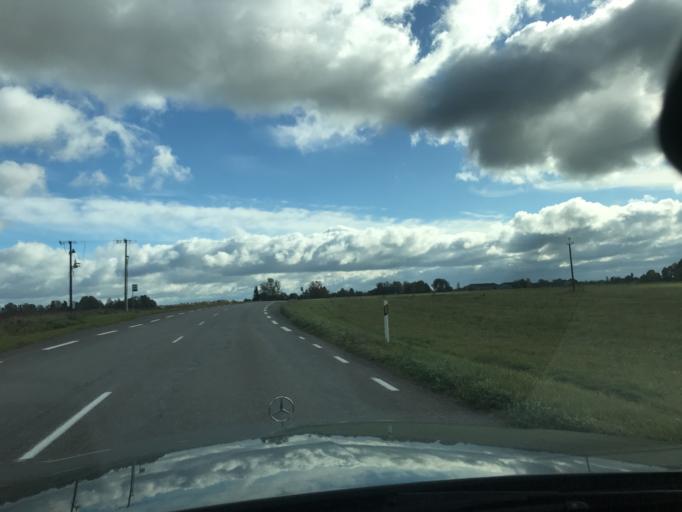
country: EE
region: Vorumaa
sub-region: Antsla vald
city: Vana-Antsla
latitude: 57.9021
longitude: 26.4717
